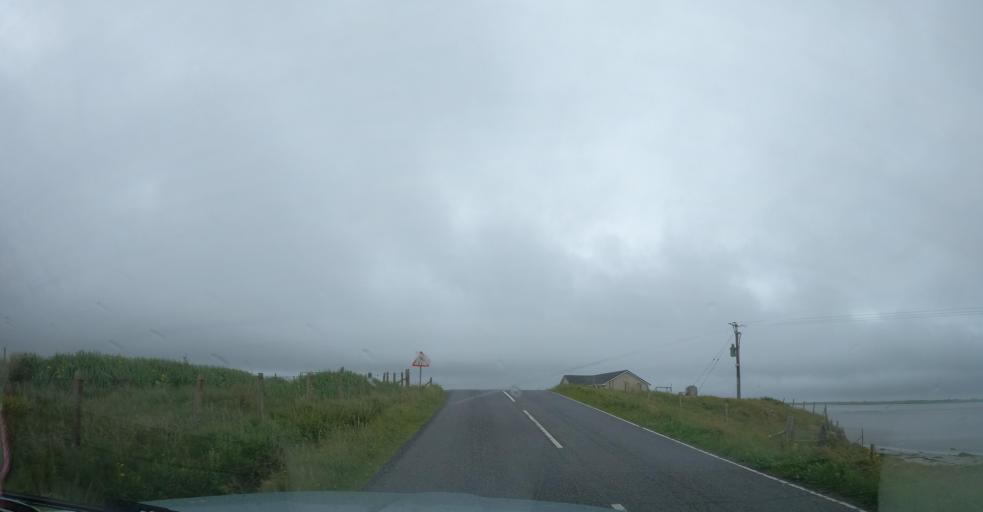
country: GB
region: Scotland
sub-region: Eilean Siar
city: Isle of North Uist
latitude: 57.5594
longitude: -7.3688
